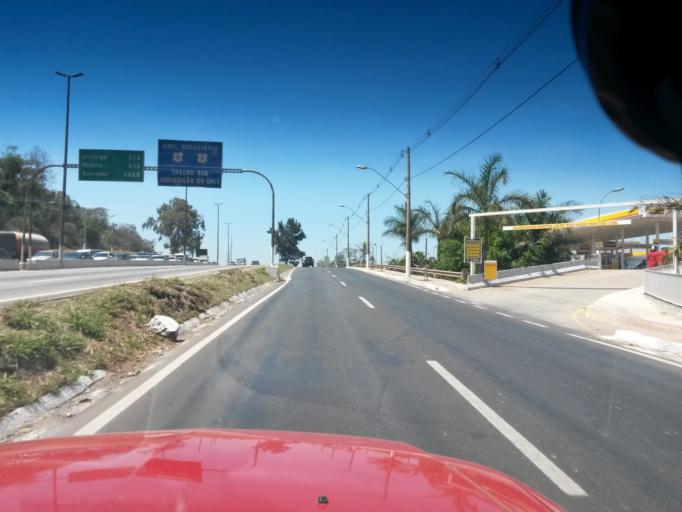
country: BR
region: Minas Gerais
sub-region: Belo Horizonte
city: Belo Horizonte
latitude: -19.8917
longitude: -43.9751
